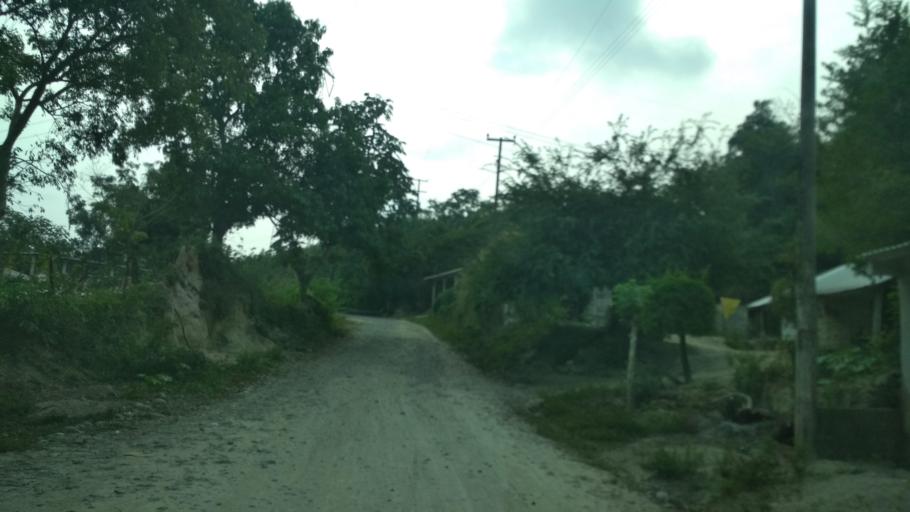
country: MM
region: Kayah
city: Loikaw
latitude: 20.2199
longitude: 97.2848
